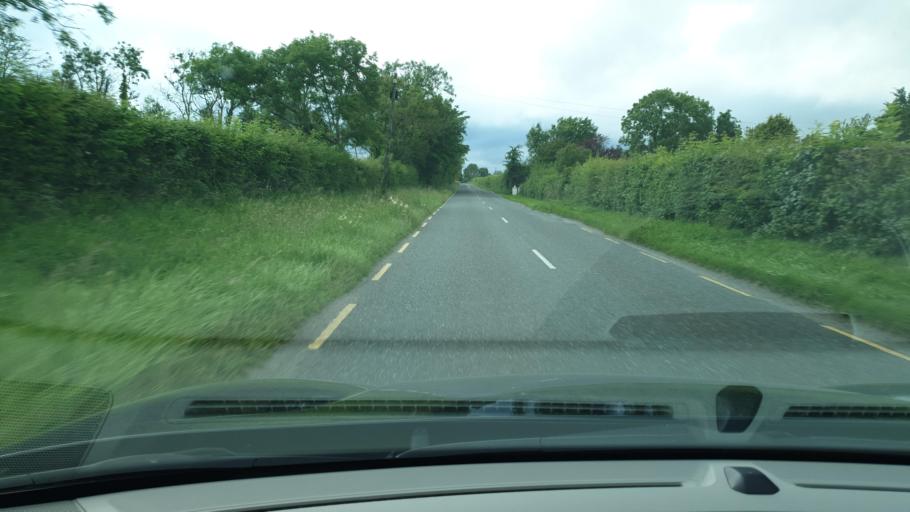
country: IE
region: Leinster
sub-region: An Mhi
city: Dunshaughlin
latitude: 53.5393
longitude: -6.5031
